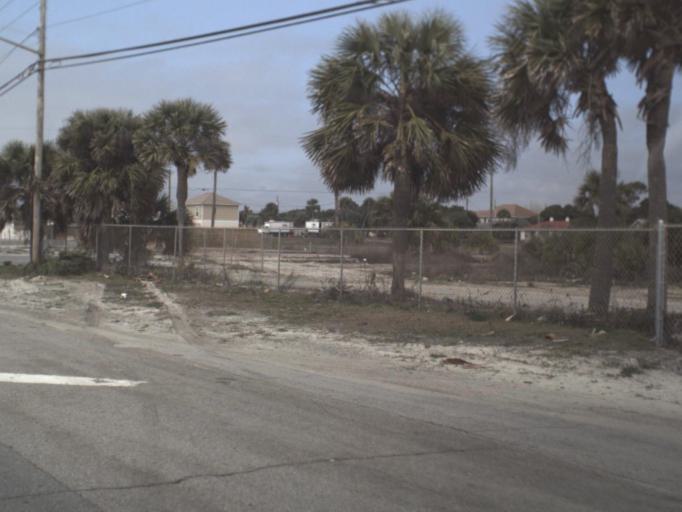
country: US
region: Florida
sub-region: Bay County
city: Panama City Beach
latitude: 30.1997
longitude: -85.8469
